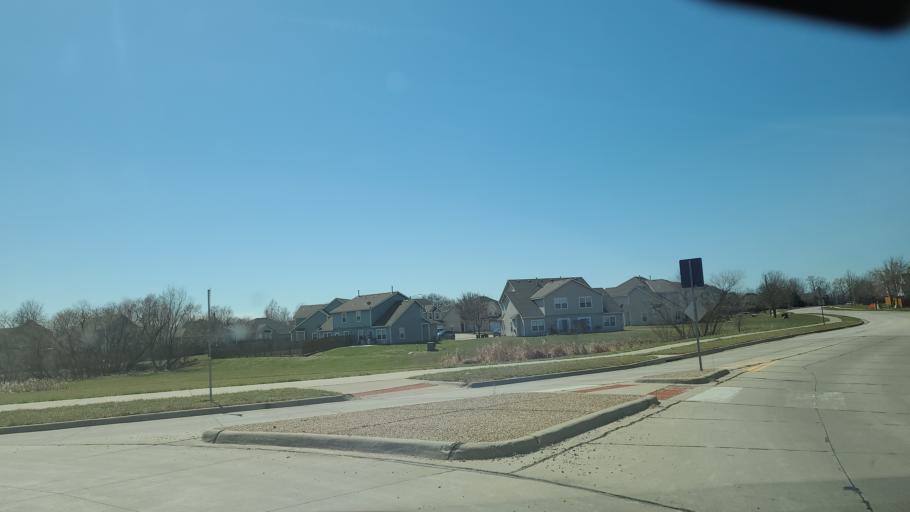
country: US
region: Kansas
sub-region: Douglas County
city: Lawrence
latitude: 38.9393
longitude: -95.2051
